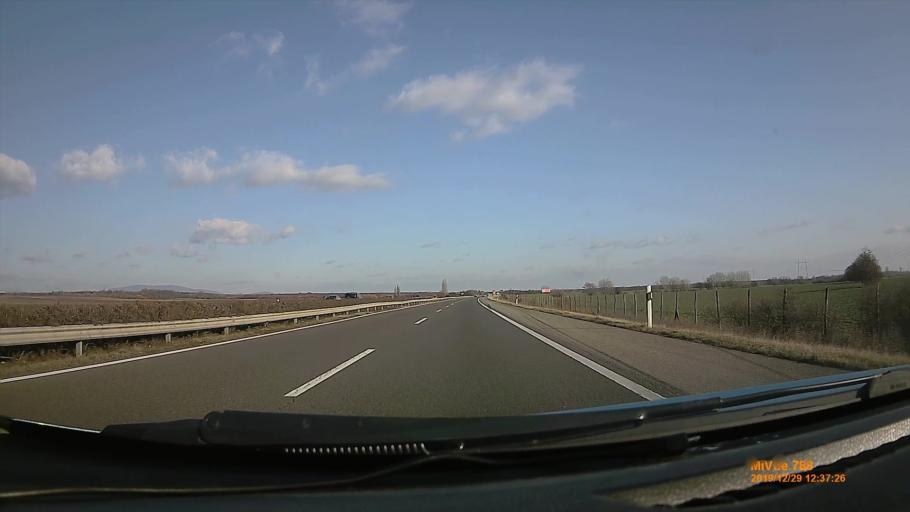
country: HU
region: Heves
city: Gyongyospata
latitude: 47.8124
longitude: 19.7811
